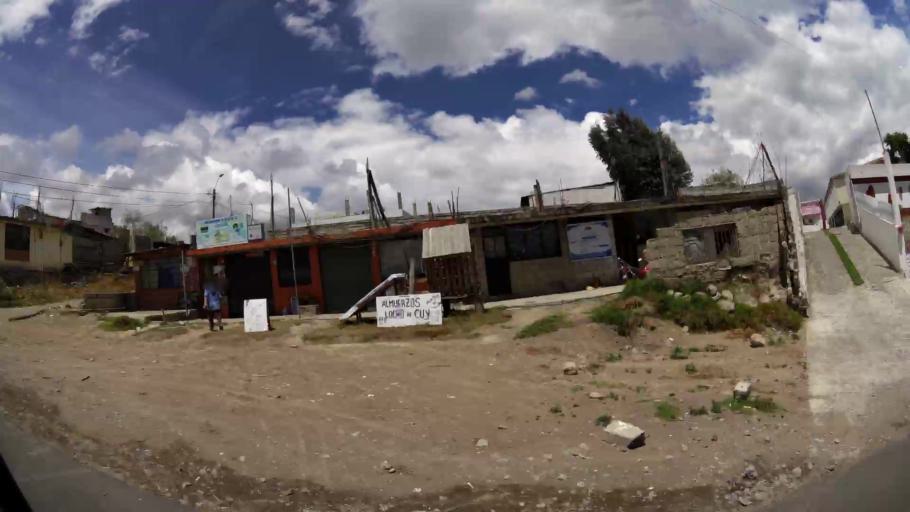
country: EC
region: Tungurahua
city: Ambato
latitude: -1.2740
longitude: -78.5902
